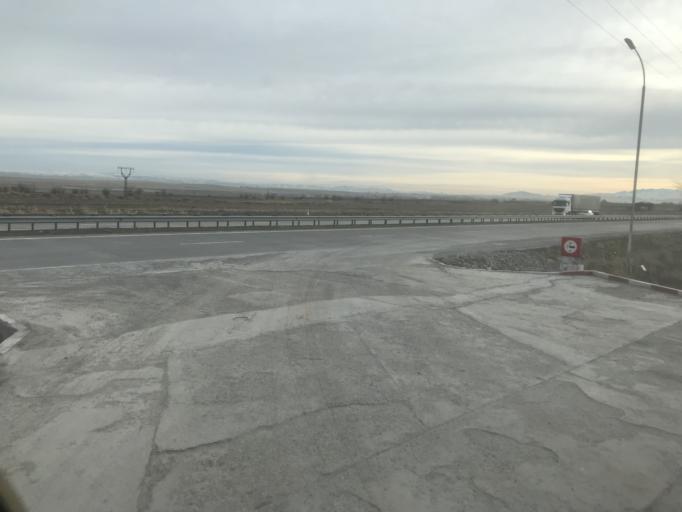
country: KZ
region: Ongtustik Qazaqstan
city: Shymkent
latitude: 42.4624
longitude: 69.5760
